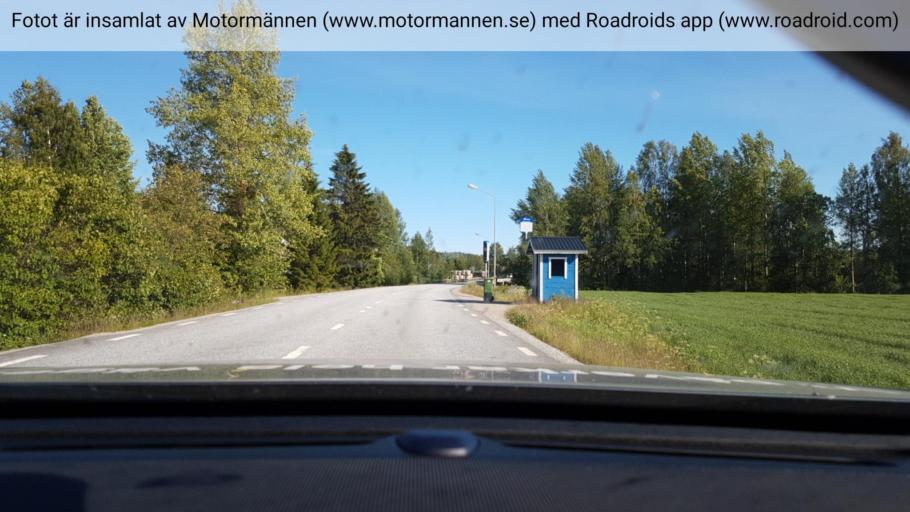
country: SE
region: Vaesterbotten
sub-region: Vindelns Kommun
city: Vindeln
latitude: 64.1667
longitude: 19.4958
